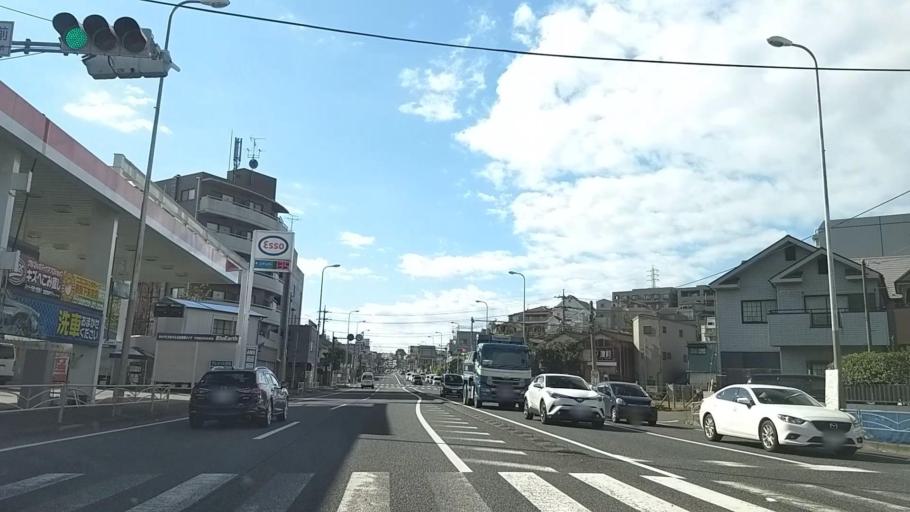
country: JP
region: Kanagawa
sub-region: Kawasaki-shi
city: Kawasaki
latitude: 35.5203
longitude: 139.6709
